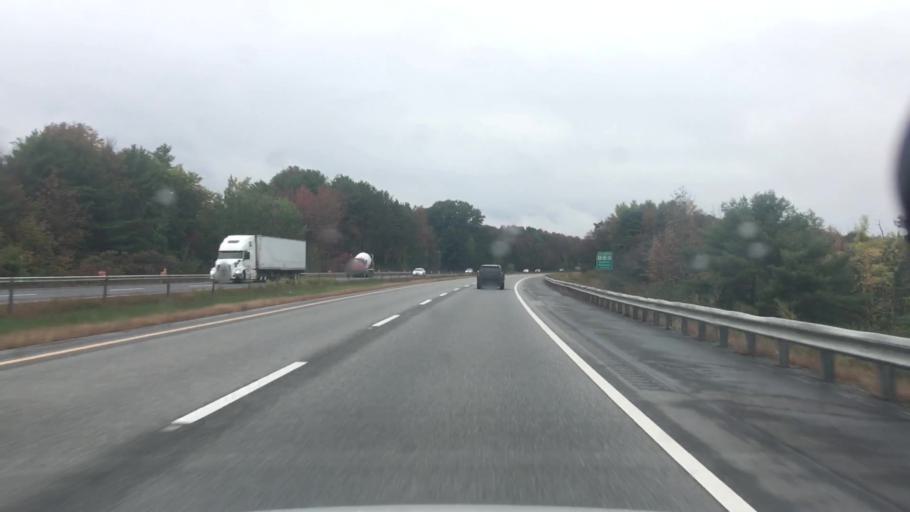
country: US
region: Maine
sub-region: Kennebec County
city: Augusta
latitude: 44.3240
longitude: -69.8147
